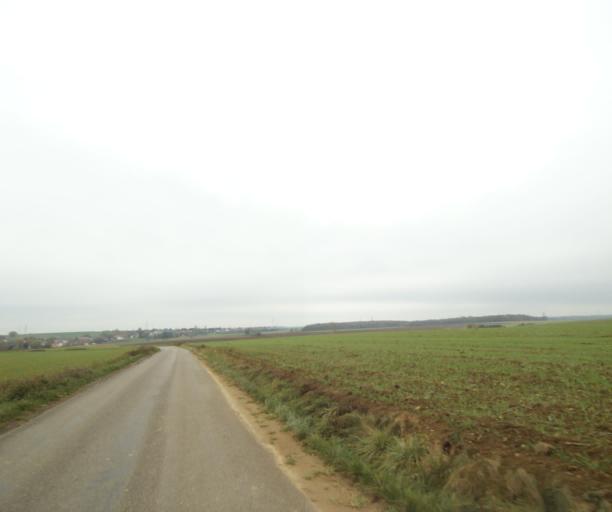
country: FR
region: Lorraine
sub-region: Departement de Meurthe-et-Moselle
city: Briey
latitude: 49.2581
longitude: 5.9105
